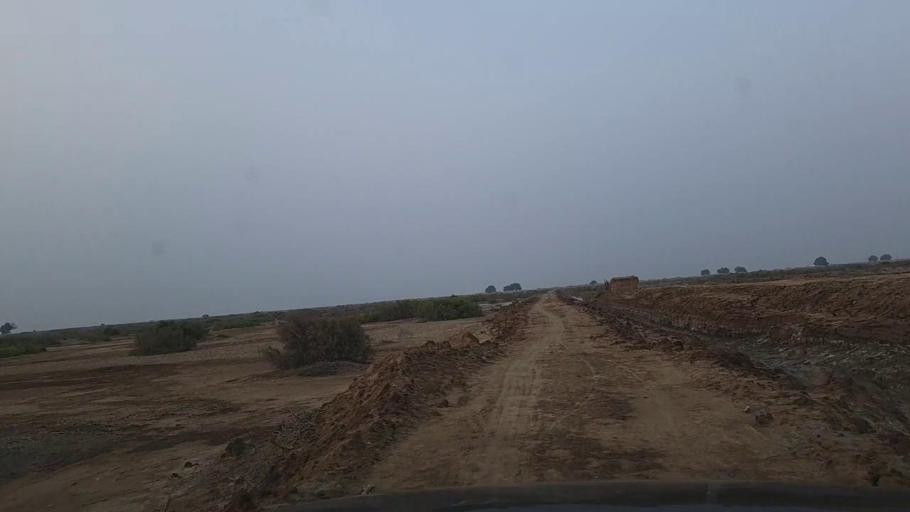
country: PK
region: Sindh
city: Gharo
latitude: 24.7475
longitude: 67.7203
